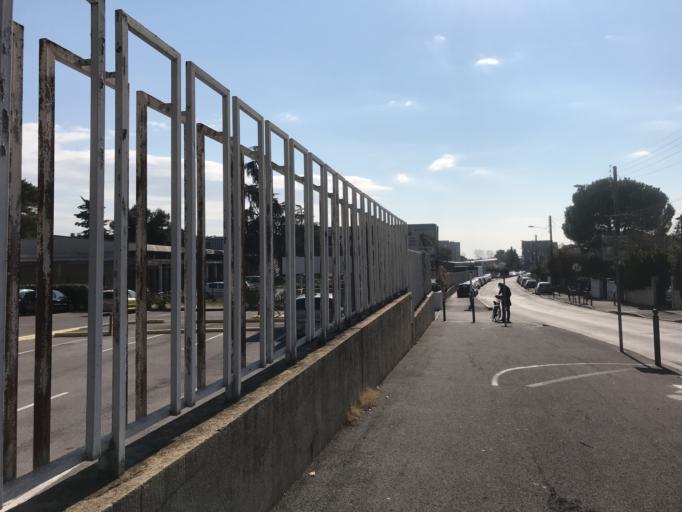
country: FR
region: Languedoc-Roussillon
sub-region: Departement de l'Herault
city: Montpellier
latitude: 43.6347
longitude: 3.8599
